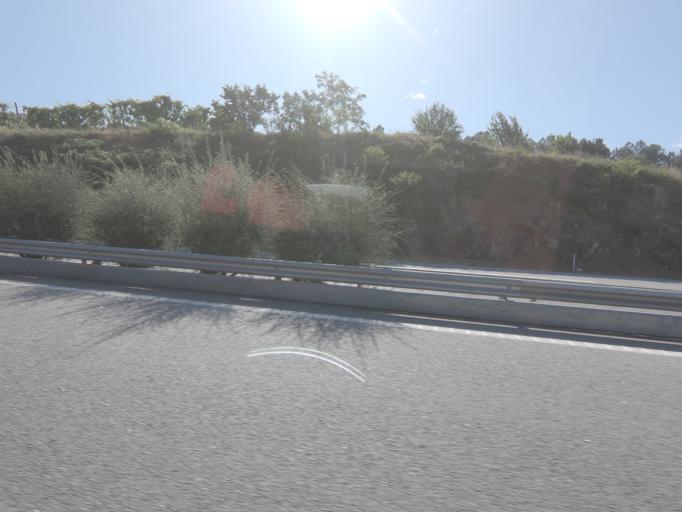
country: PT
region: Porto
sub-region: Marco de Canaveses
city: Marco de Canavezes
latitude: 41.2213
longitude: -8.1490
